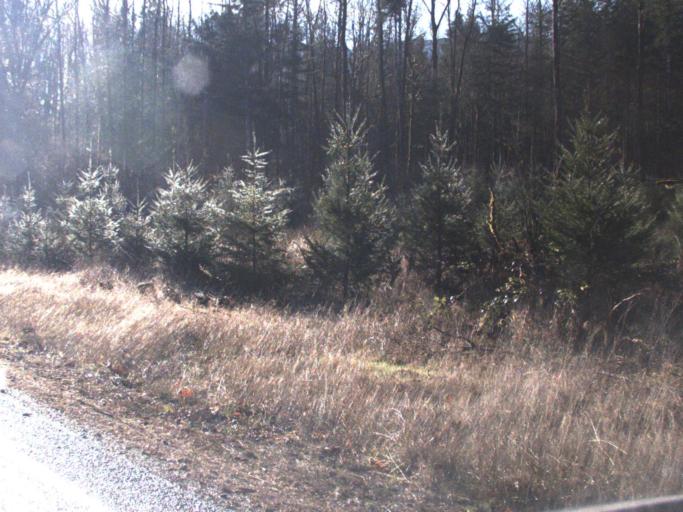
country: US
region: Washington
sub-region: Snohomish County
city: Darrington
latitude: 48.4706
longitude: -121.5886
